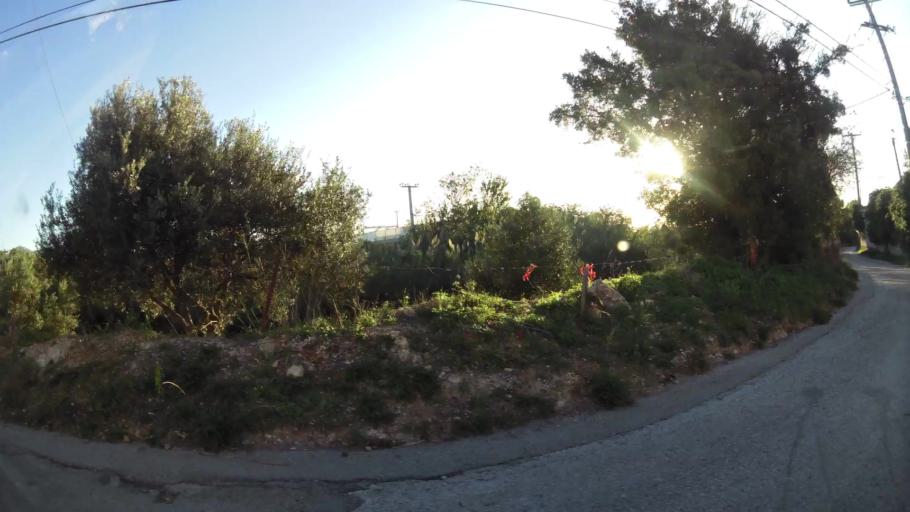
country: GR
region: Attica
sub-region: Nomarchia Anatolikis Attikis
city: Pallini
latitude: 37.9973
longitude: 23.8867
